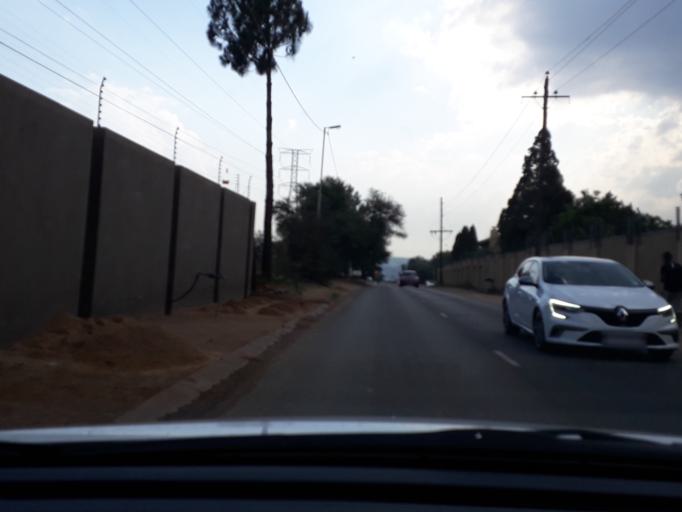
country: ZA
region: Gauteng
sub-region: City of Johannesburg Metropolitan Municipality
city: Diepsloot
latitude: -26.0019
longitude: 27.9885
